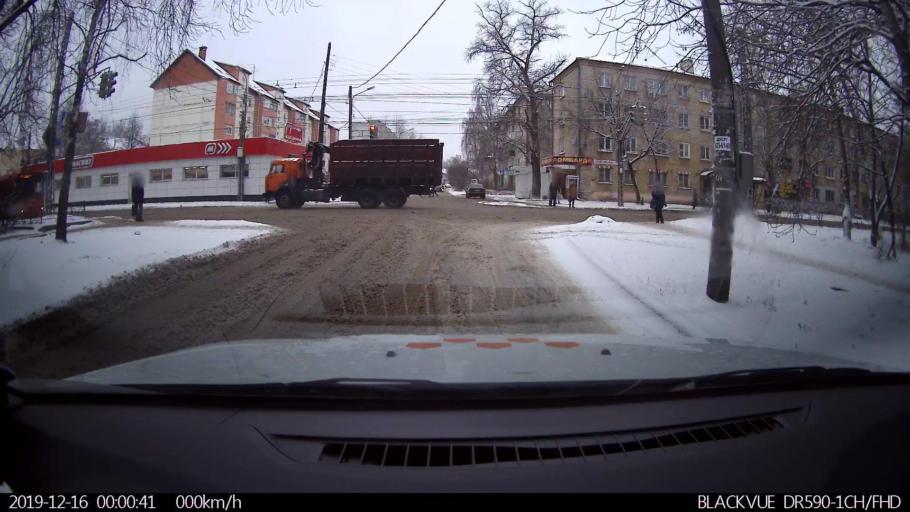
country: RU
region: Nizjnij Novgorod
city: Neklyudovo
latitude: 56.3598
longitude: 43.8487
